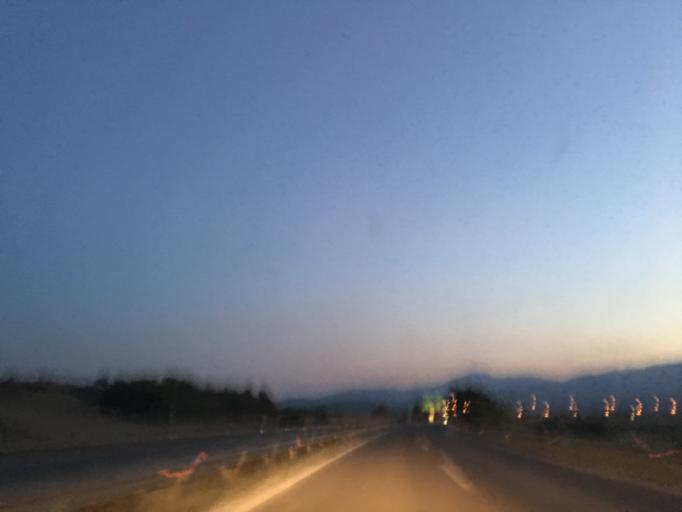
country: MK
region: Petrovec
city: Petrovec
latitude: 41.9455
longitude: 21.6303
